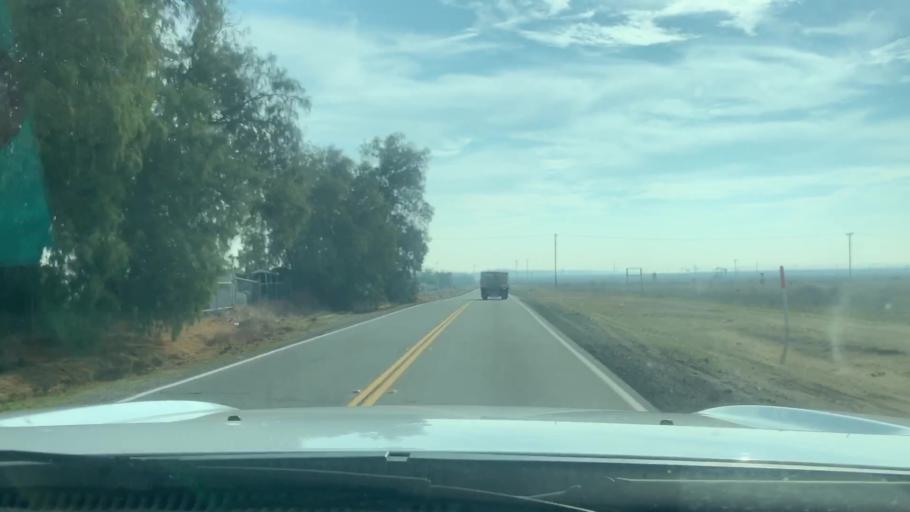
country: US
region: California
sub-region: Kern County
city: Lost Hills
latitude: 35.5384
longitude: -119.7735
